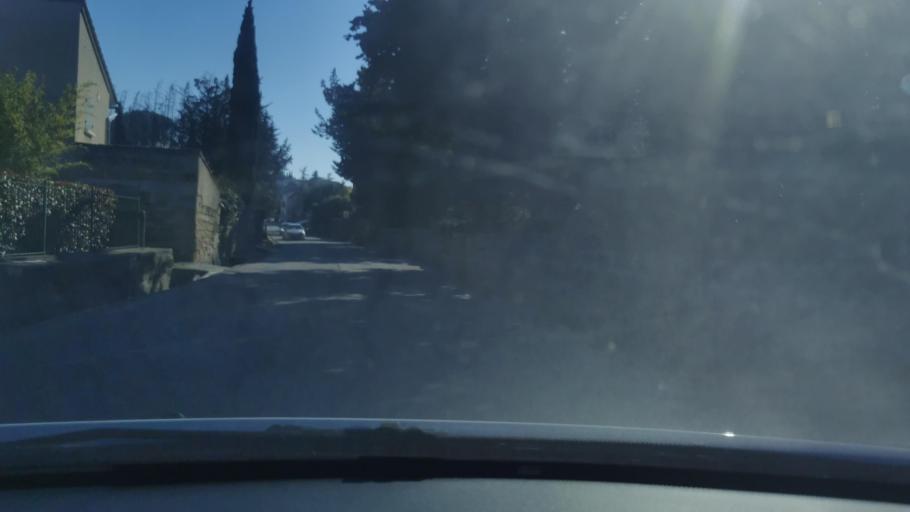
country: FR
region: Languedoc-Roussillon
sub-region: Departement du Gard
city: Saint-Quentin-la-Poterie
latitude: 44.0477
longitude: 4.4361
